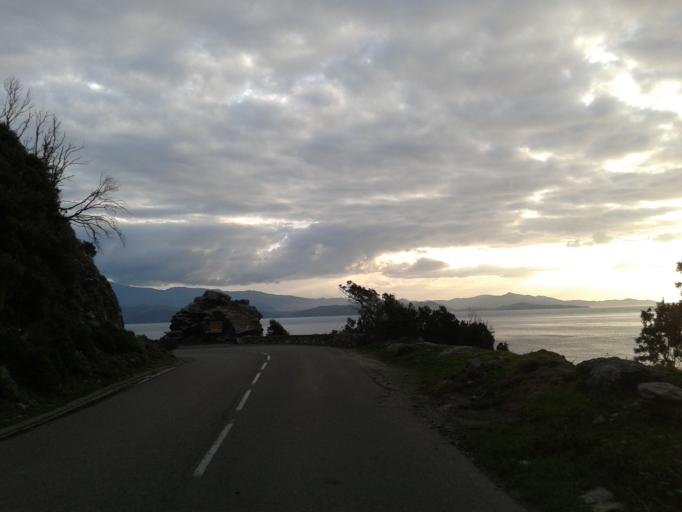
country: FR
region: Corsica
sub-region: Departement de la Haute-Corse
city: Saint-Florent
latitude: 42.7627
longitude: 9.3390
